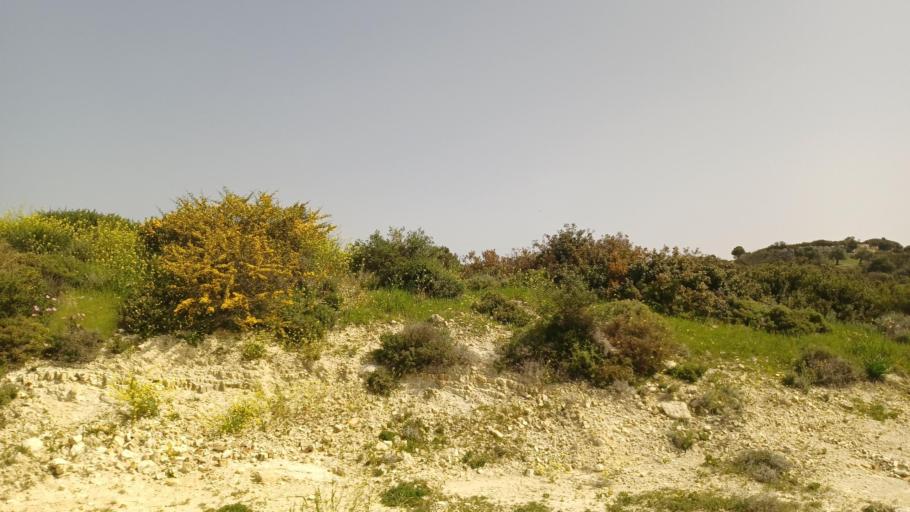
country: CY
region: Limassol
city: Pissouri
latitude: 34.7052
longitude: 32.7041
